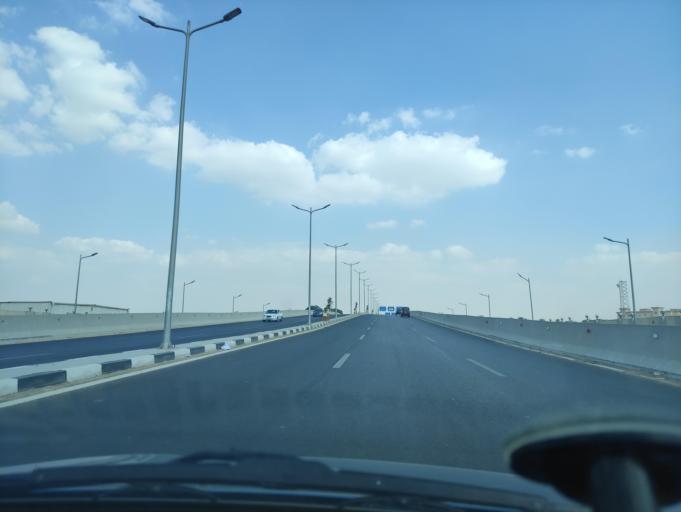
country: EG
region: Muhafazat al Qahirah
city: Cairo
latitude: 30.0410
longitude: 31.3010
